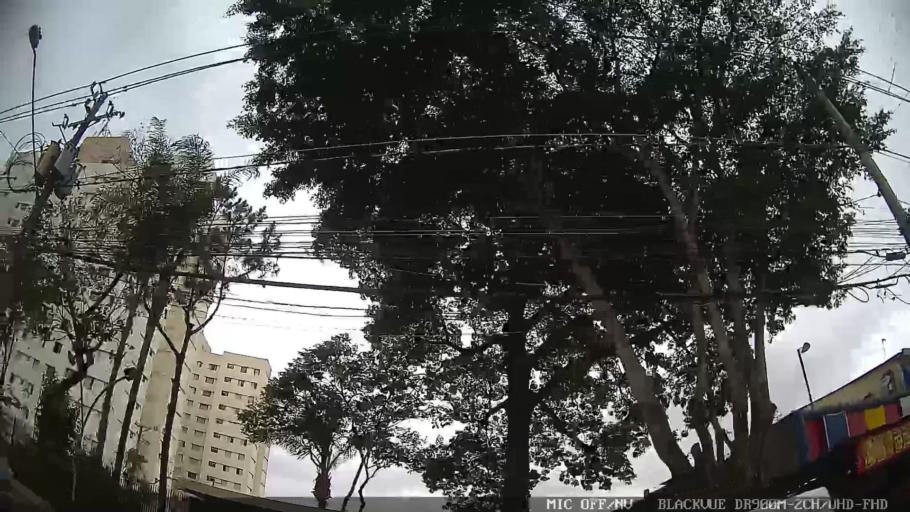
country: BR
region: Sao Paulo
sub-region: Osasco
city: Osasco
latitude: -23.4858
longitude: -46.7556
